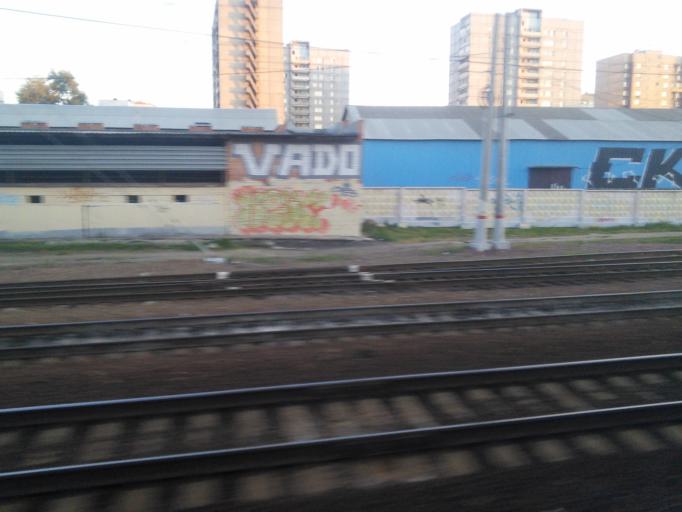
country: RU
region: Moskovskaya
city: Zheleznodorozhnyy
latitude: 55.7523
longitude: 38.0022
